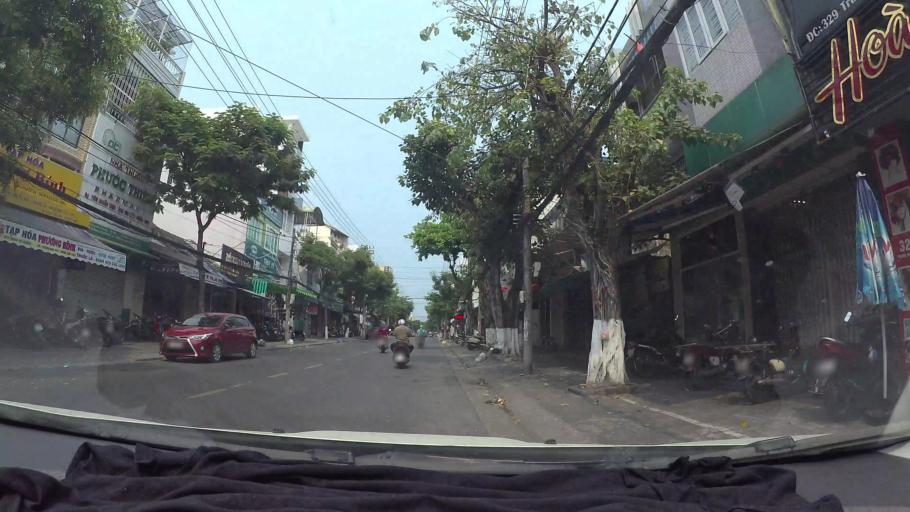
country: VN
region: Da Nang
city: Da Nang
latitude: 16.0515
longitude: 108.2165
